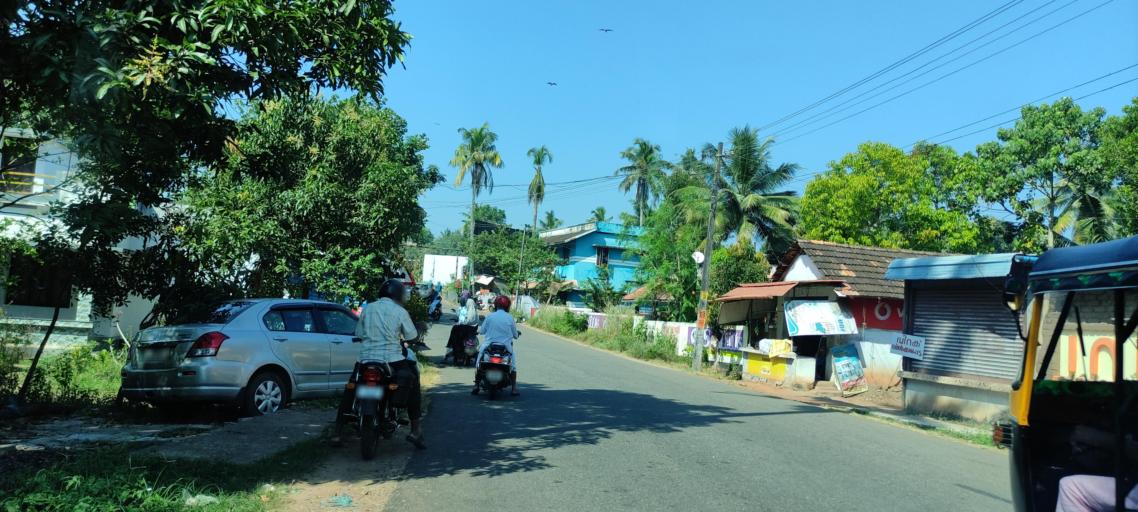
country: IN
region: Kerala
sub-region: Kollam
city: Panmana
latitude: 9.0444
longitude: 76.5788
